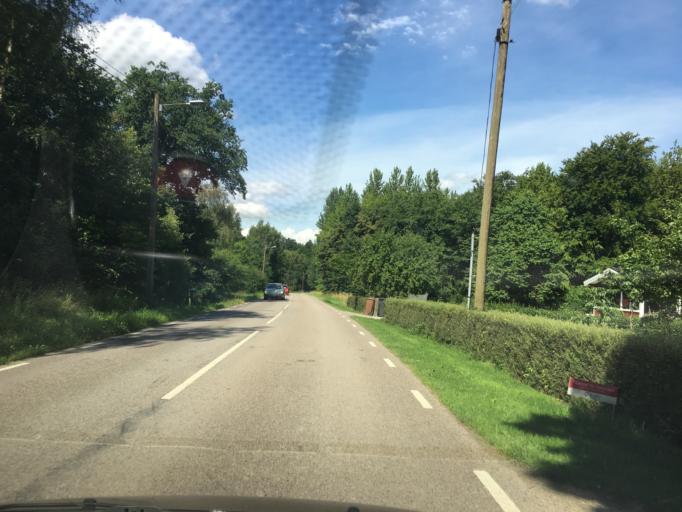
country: SE
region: Skane
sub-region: Svalovs Kommun
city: Kagerod
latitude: 55.9908
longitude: 13.1011
